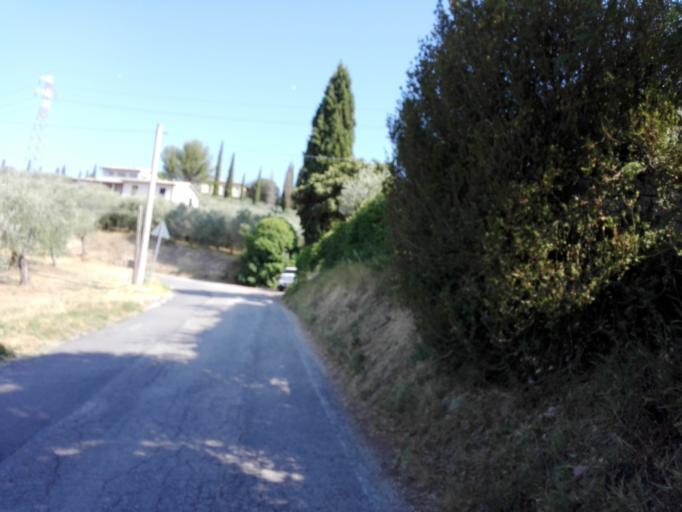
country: IT
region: Umbria
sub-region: Provincia di Perugia
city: Foligno
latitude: 42.9755
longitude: 12.7058
